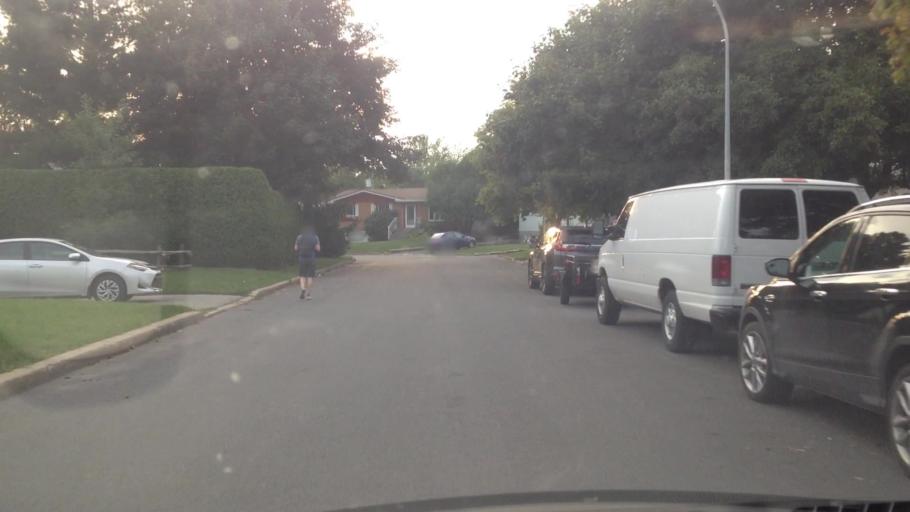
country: CA
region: Quebec
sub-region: Monteregie
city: Mercier
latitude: 45.3466
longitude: -73.7147
